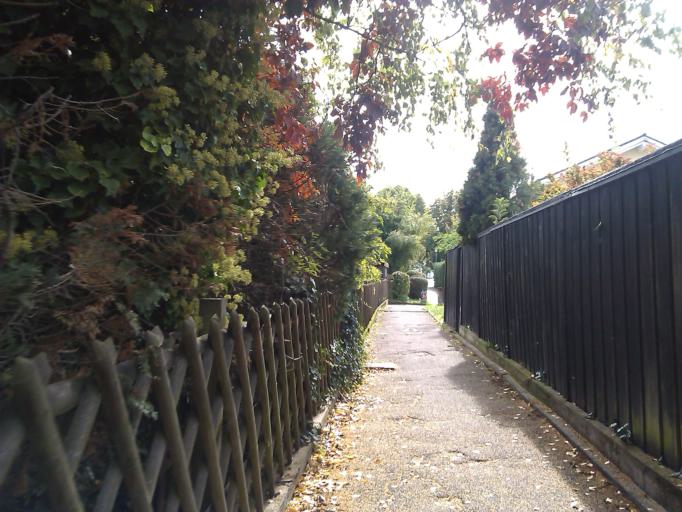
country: DE
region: Baden-Wuerttemberg
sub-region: Karlsruhe Region
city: Hemsbach
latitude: 49.5949
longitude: 8.6499
